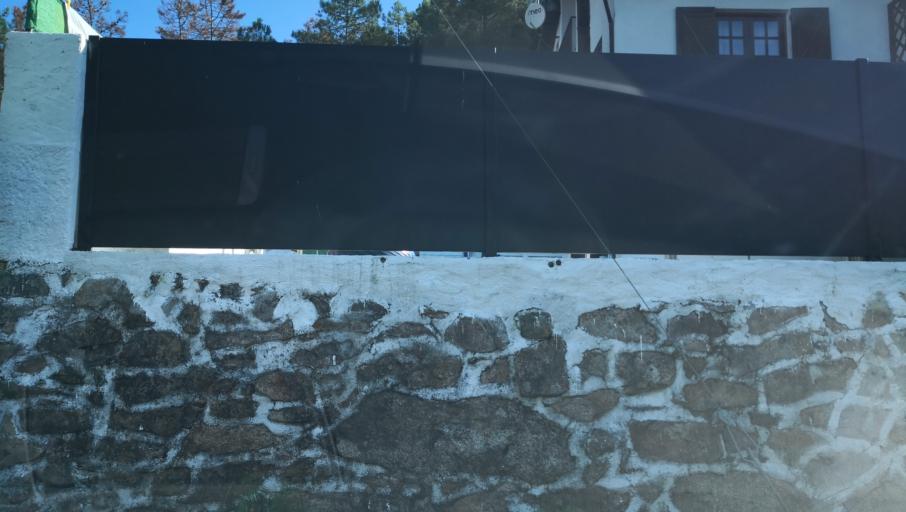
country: PT
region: Vila Real
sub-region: Vila Real
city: Vila Real
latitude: 41.3183
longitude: -7.7100
